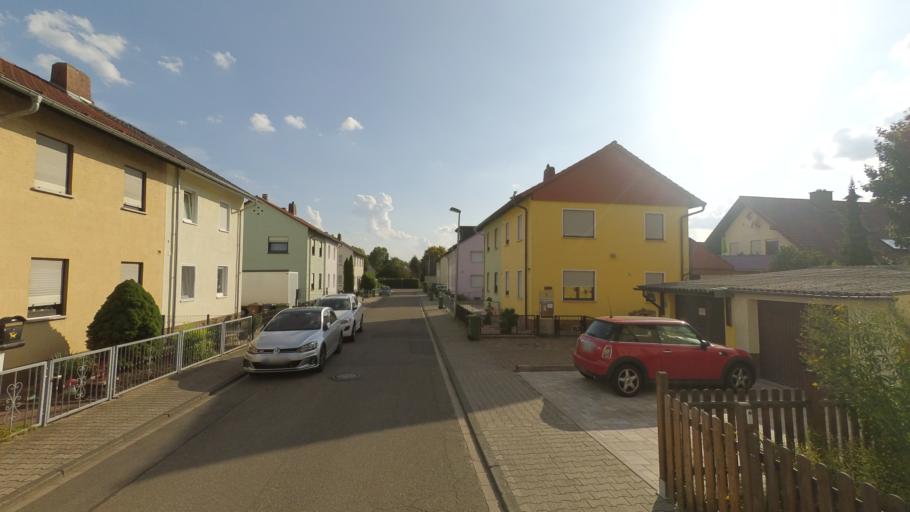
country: DE
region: Hesse
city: Lampertheim
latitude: 49.5960
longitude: 8.4574
